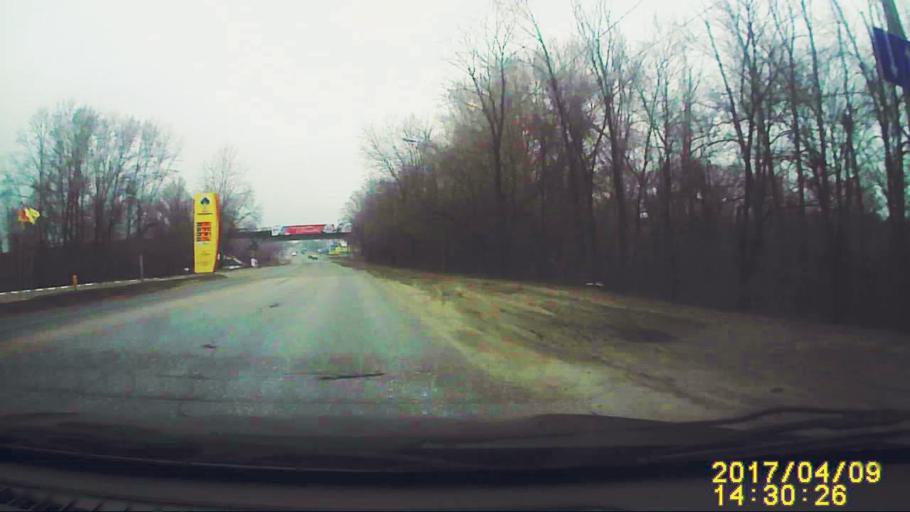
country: RU
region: Ulyanovsk
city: Novoul'yanovsk
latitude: 54.2135
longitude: 48.2975
